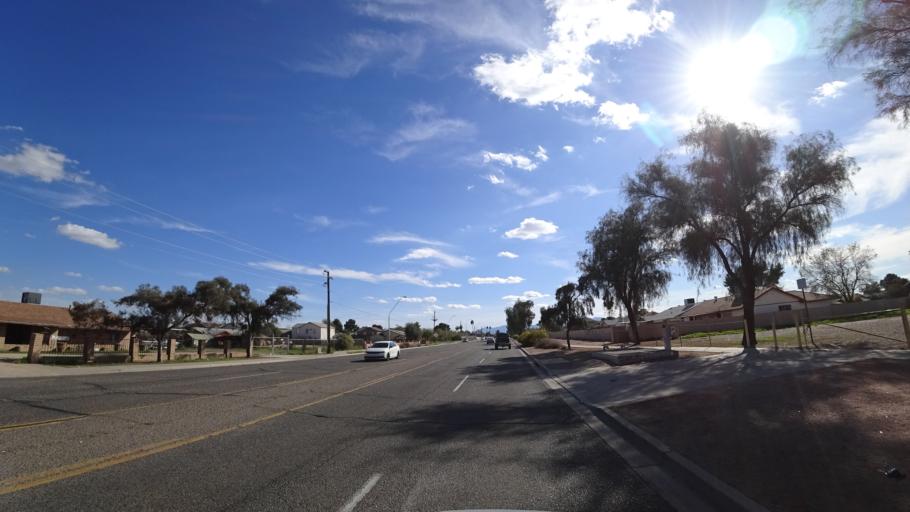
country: US
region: Arizona
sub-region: Maricopa County
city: Glendale
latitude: 33.5076
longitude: -112.2206
